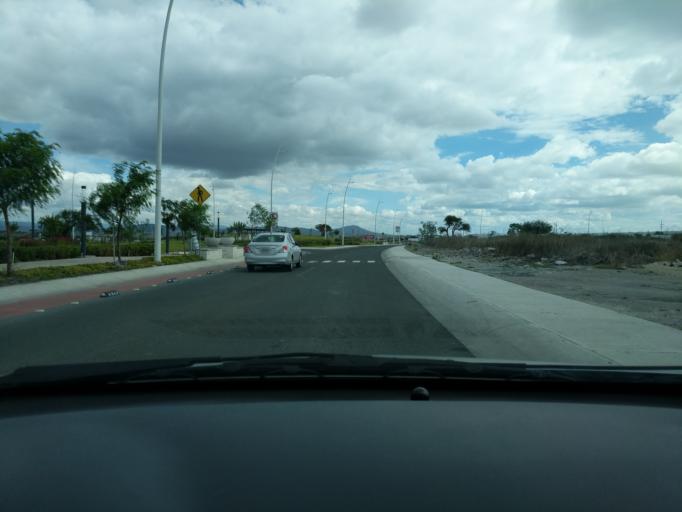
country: MX
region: Queretaro
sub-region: El Marques
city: La Pradera
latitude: 20.6595
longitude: -100.3132
